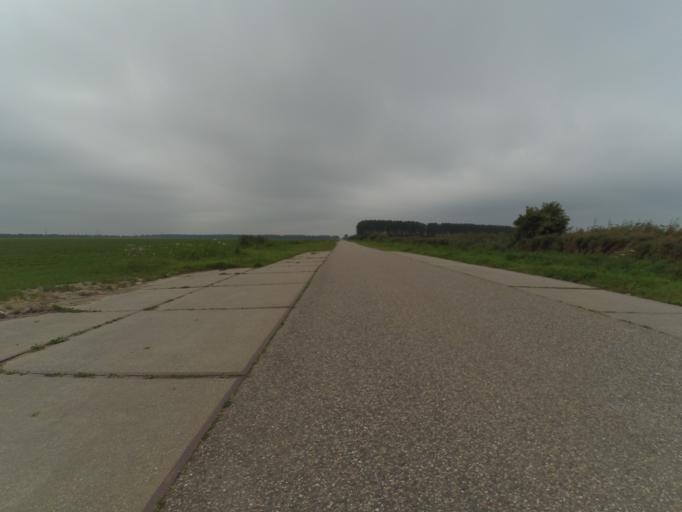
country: NL
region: Flevoland
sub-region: Gemeente Lelystad
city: Lelystad
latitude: 52.4870
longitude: 5.4794
